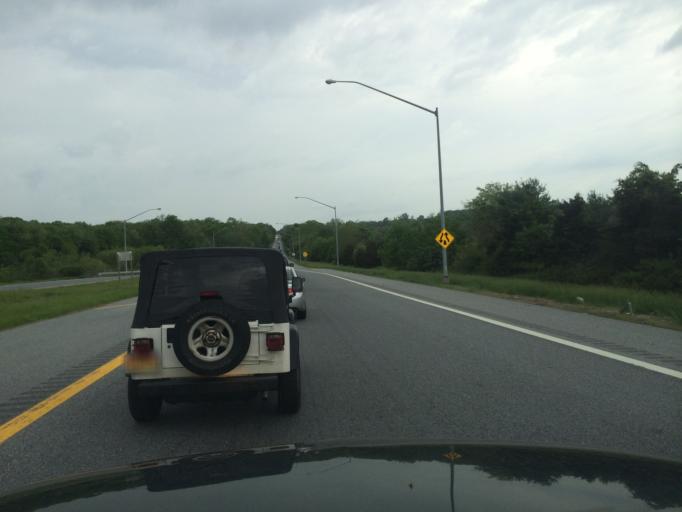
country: US
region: Maryland
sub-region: Howard County
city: Highland
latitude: 39.2106
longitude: -76.9474
